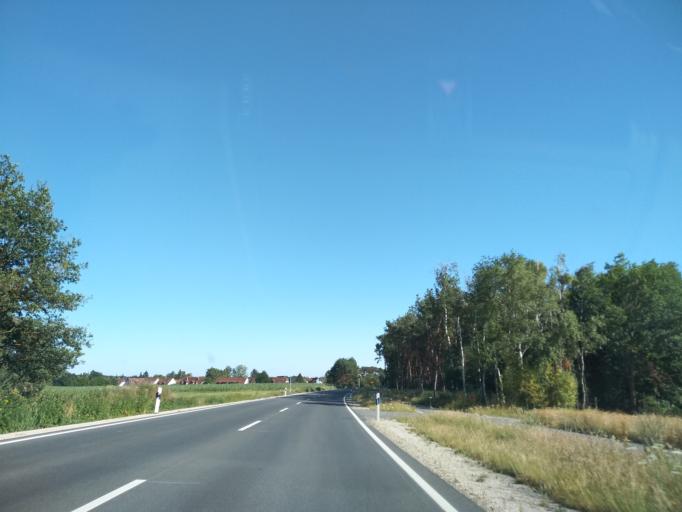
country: DE
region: Bavaria
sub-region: Regierungsbezirk Mittelfranken
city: Hessdorf
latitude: 49.6361
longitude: 10.9304
